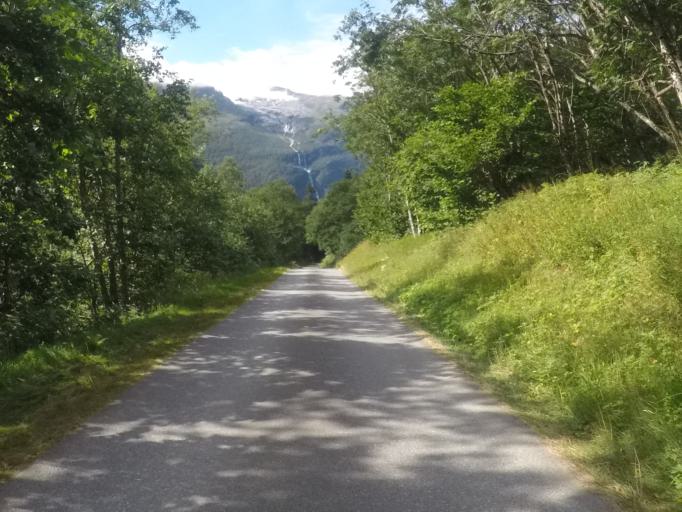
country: NO
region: Sogn og Fjordane
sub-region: Stryn
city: Stryn
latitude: 61.7657
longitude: 7.0384
